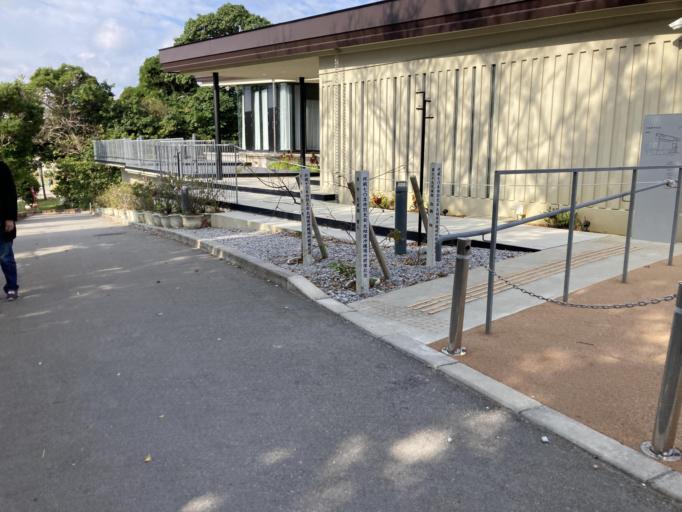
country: JP
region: Okinawa
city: Naha-shi
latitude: 26.2023
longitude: 127.6765
